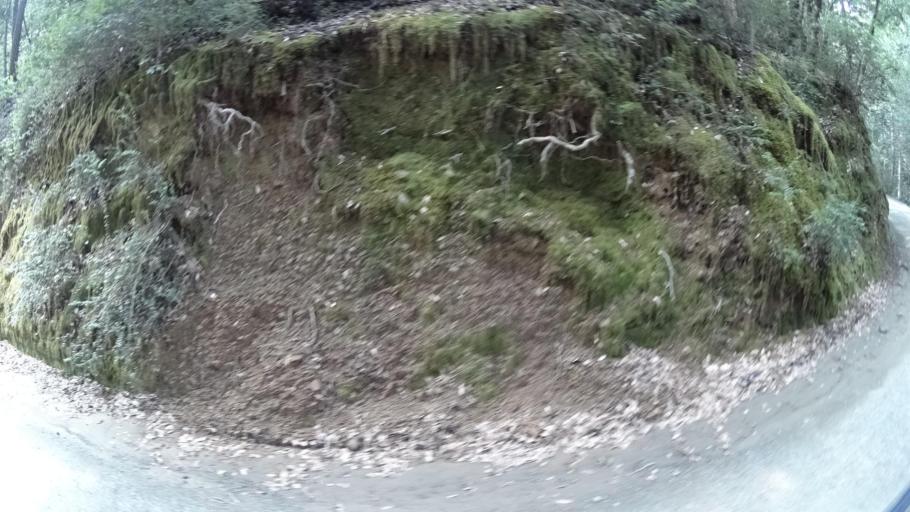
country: US
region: California
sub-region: Humboldt County
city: Redway
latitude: 40.0302
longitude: -123.8353
